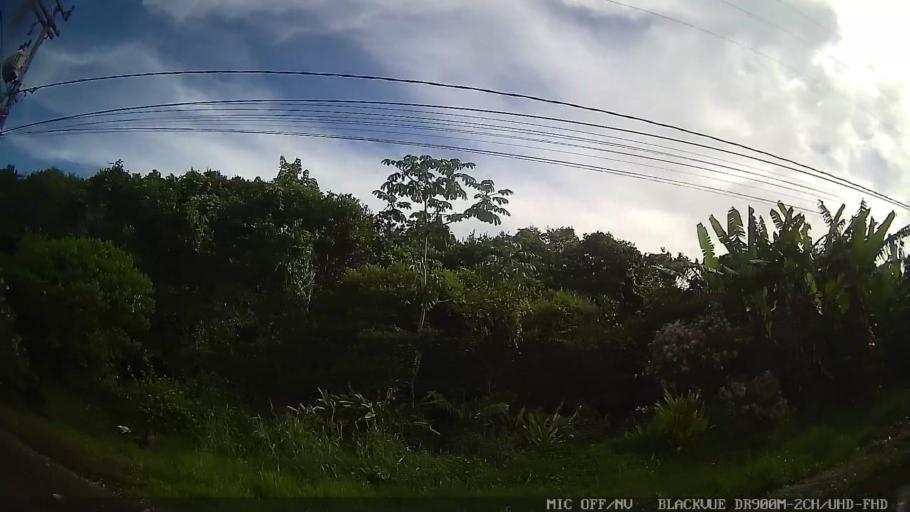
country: BR
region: Sao Paulo
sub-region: Itanhaem
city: Itanhaem
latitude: -24.2122
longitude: -46.8748
